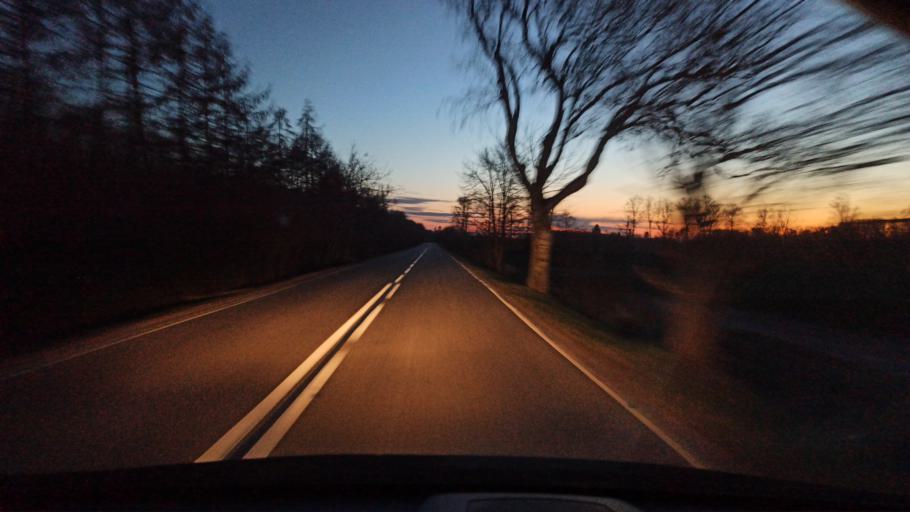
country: PL
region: Warmian-Masurian Voivodeship
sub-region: Powiat elblaski
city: Gronowo Gorne
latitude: 54.1707
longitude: 19.5024
